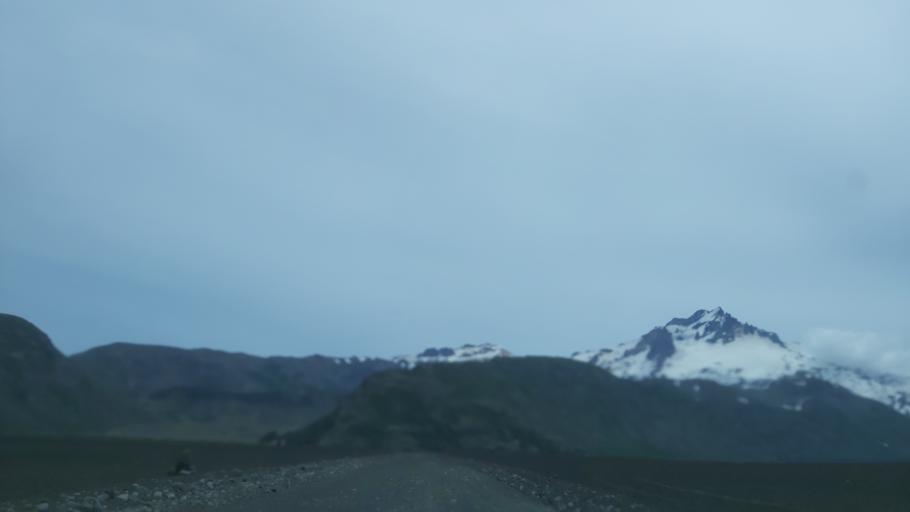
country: AR
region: Neuquen
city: Andacollo
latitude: -37.4597
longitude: -71.3053
